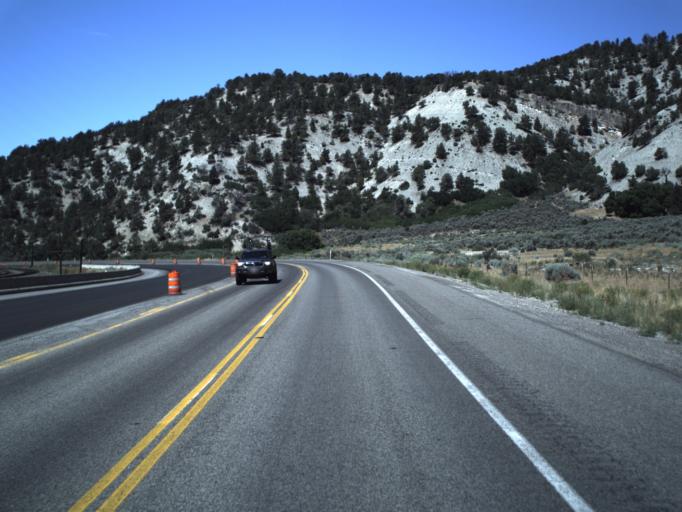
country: US
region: Utah
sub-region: Utah County
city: Mapleton
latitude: 39.9541
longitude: -111.2647
